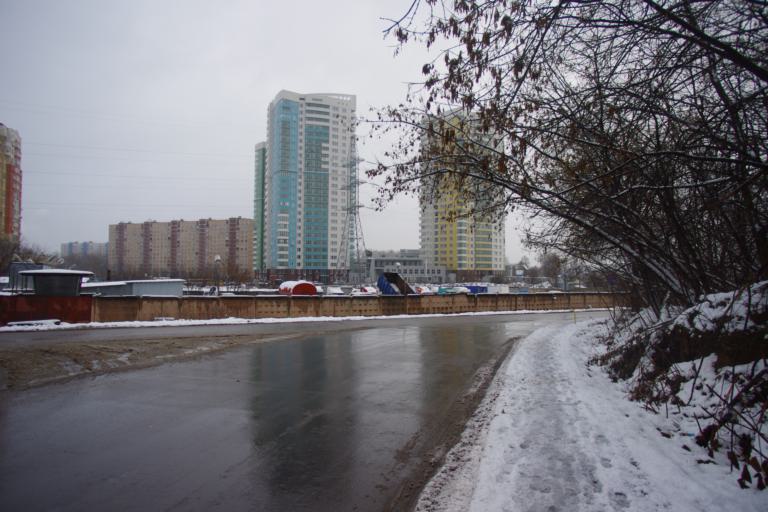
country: RU
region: Moskovskaya
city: Krasnogorsk
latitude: 55.8056
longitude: 37.3191
